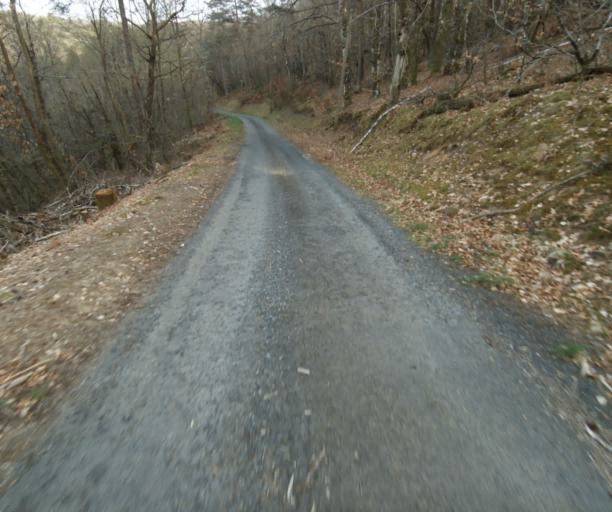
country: FR
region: Limousin
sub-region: Departement de la Correze
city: Correze
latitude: 45.3617
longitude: 1.8293
